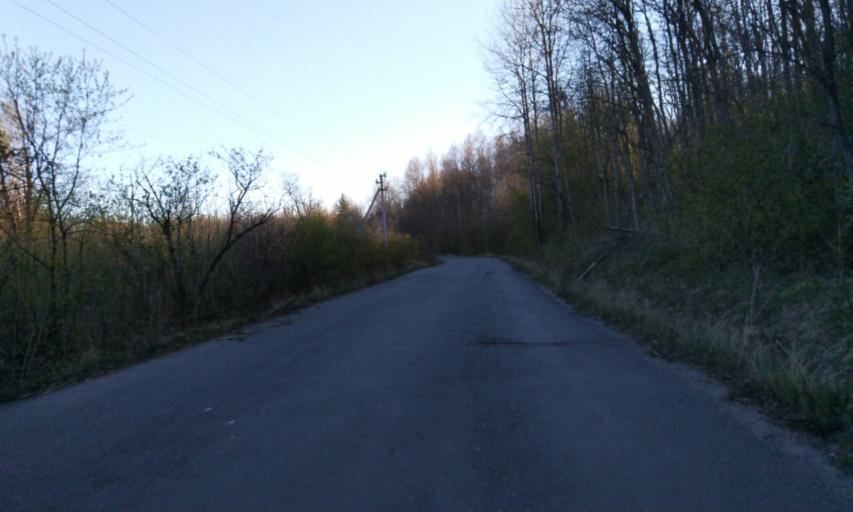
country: RU
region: Leningrad
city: Toksovo
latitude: 60.1429
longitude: 30.5721
